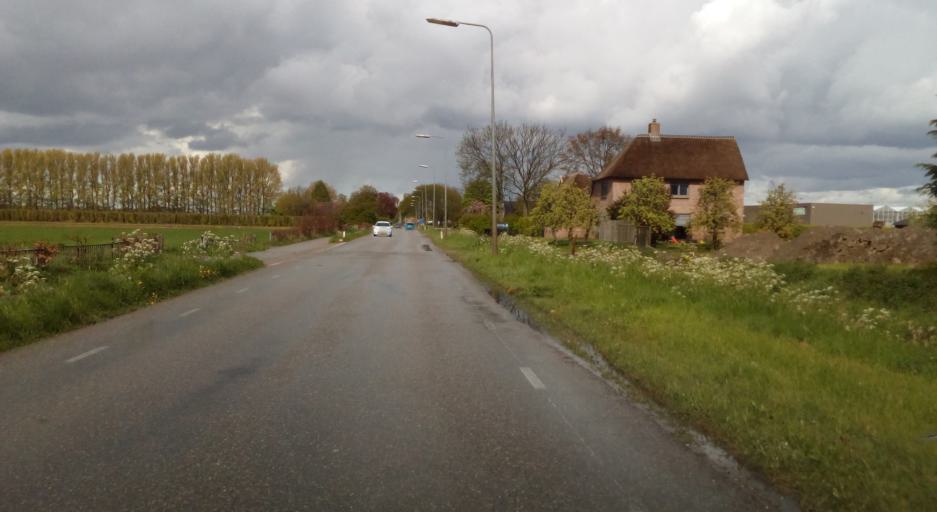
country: NL
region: South Holland
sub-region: Gemeente Zwijndrecht
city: Zwijndrecht
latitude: 51.8363
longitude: 4.6069
